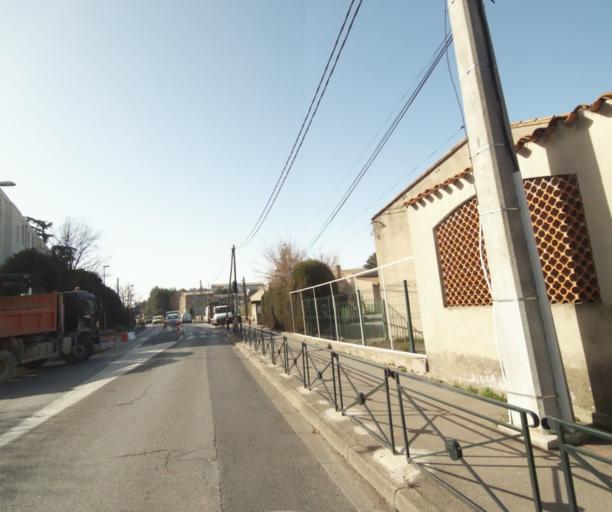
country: FR
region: Provence-Alpes-Cote d'Azur
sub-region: Departement des Bouches-du-Rhone
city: Aix-en-Provence
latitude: 43.5415
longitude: 5.4542
